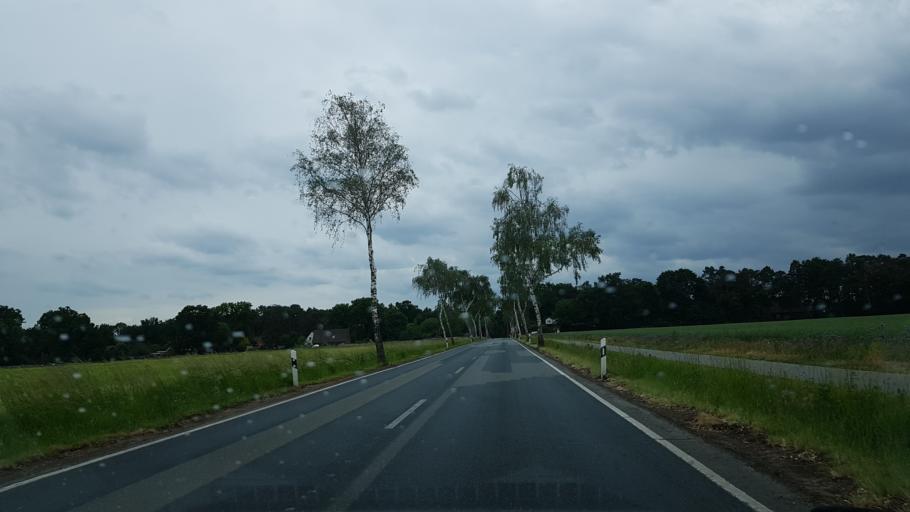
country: DE
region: Lower Saxony
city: Celle
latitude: 52.6411
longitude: 10.0600
